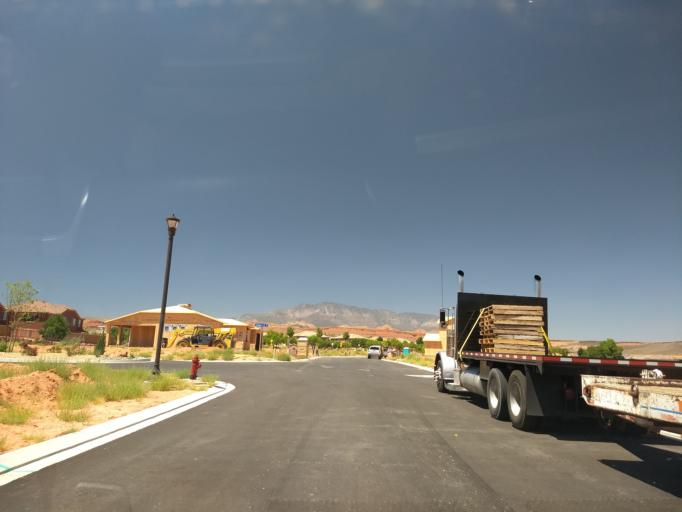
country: US
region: Utah
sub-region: Washington County
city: Washington
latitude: 37.1357
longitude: -113.4833
